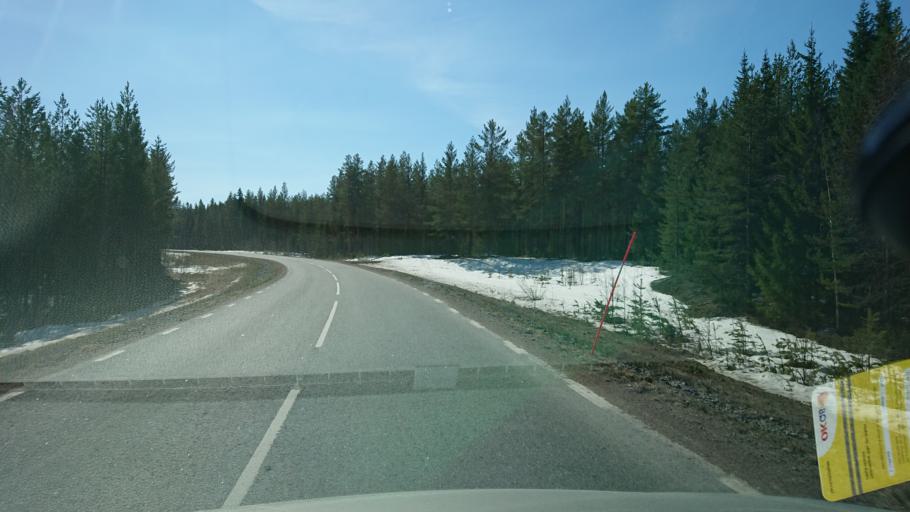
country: SE
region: Vaesternorrland
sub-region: Solleftea Kommun
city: As
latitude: 63.6715
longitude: 16.4294
